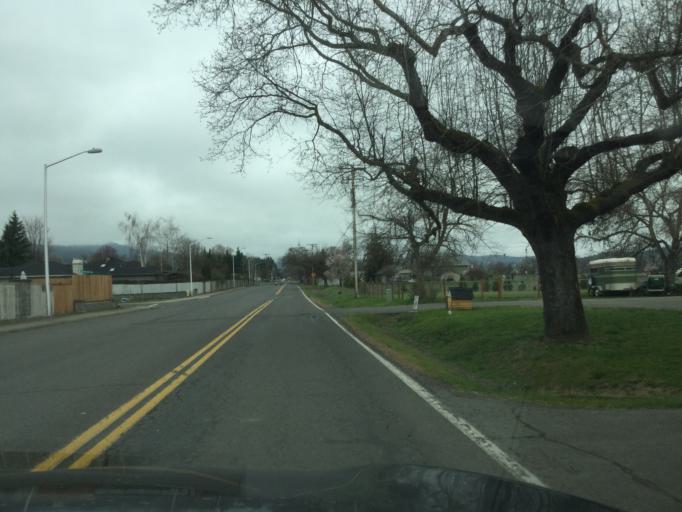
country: US
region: Oregon
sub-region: Jackson County
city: Central Point
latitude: 42.3894
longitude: -122.9294
